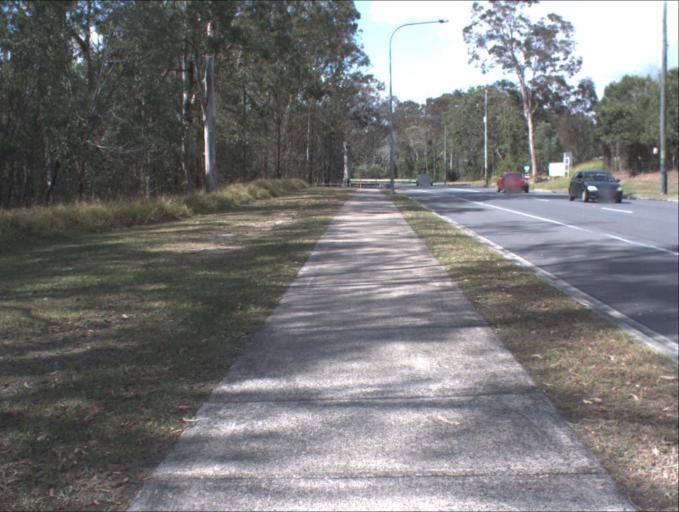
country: AU
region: Queensland
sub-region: Logan
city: Slacks Creek
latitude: -27.6543
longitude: 153.1409
